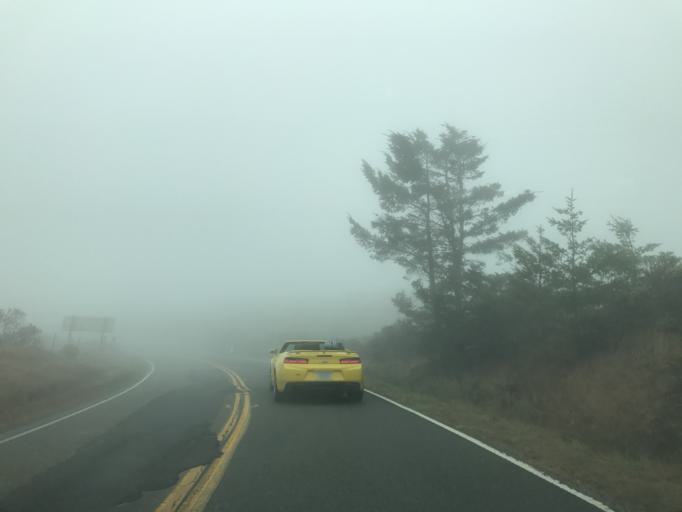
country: US
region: California
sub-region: Sonoma County
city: Monte Rio
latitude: 38.4781
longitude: -123.1615
